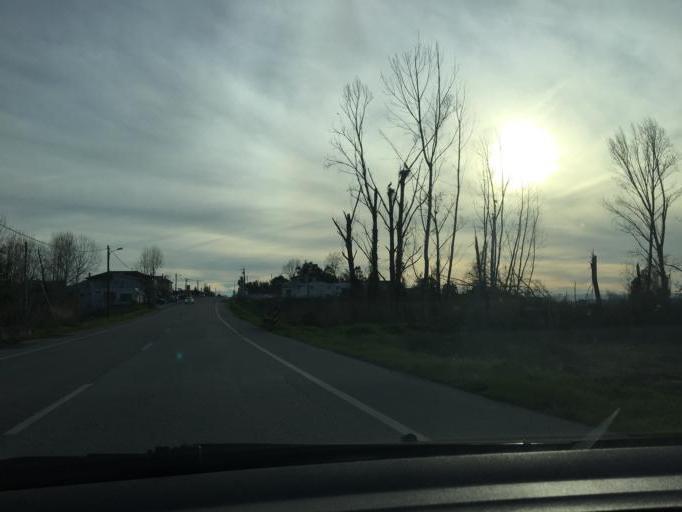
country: PT
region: Coimbra
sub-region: Montemor-O-Velho
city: Arazede
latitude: 40.2188
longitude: -8.5888
